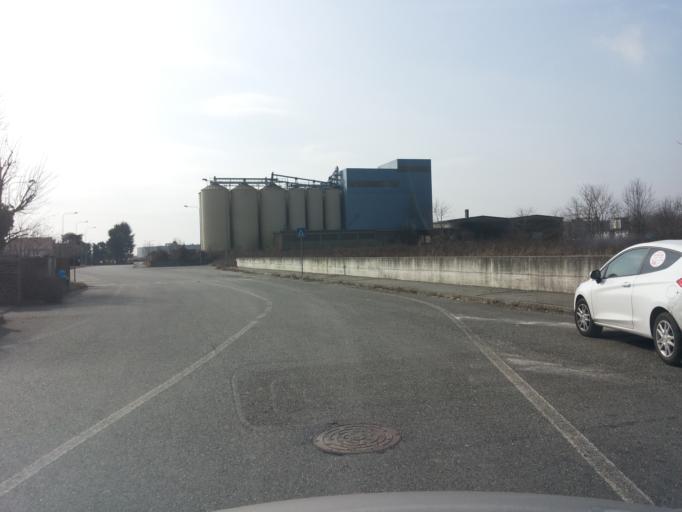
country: IT
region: Piedmont
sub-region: Provincia di Vercelli
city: Santhia
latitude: 45.3787
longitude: 8.1517
